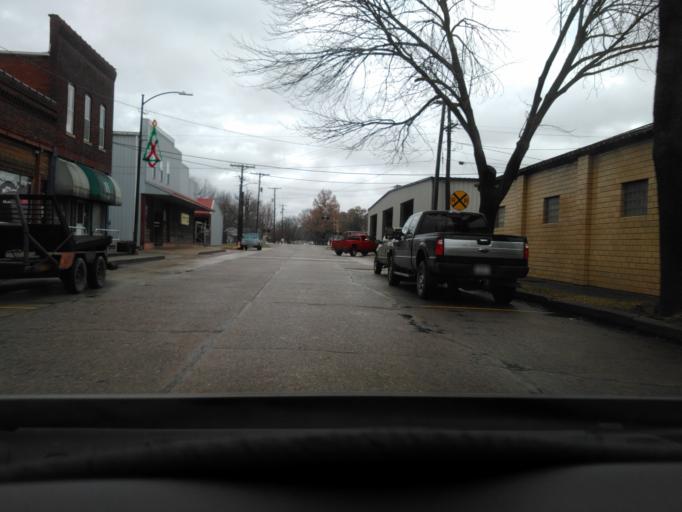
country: US
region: Illinois
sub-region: Effingham County
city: Altamont
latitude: 39.0604
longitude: -88.7496
